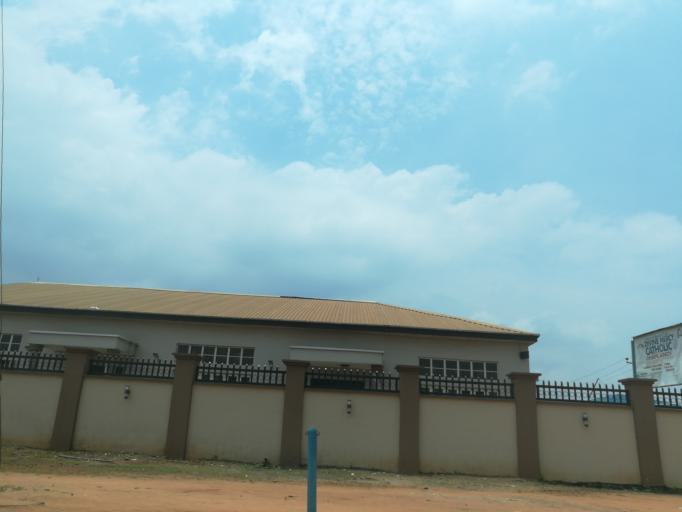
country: NG
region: Lagos
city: Ikorodu
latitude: 6.6260
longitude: 3.5482
